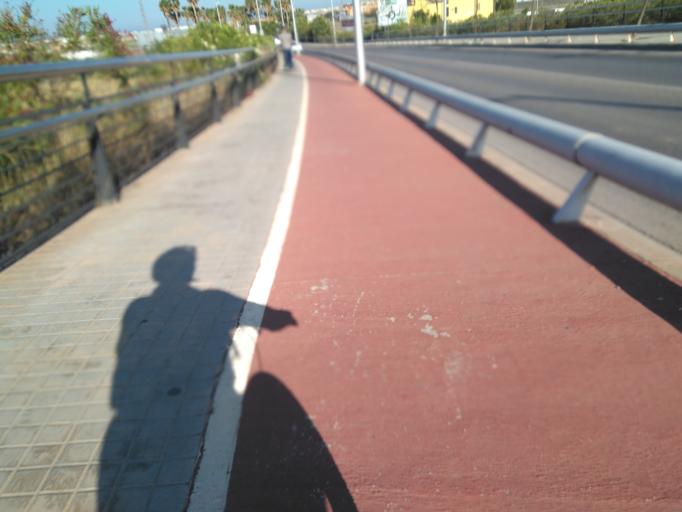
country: ES
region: Valencia
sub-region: Provincia de Valencia
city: Burjassot
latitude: 39.5036
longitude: -0.4013
